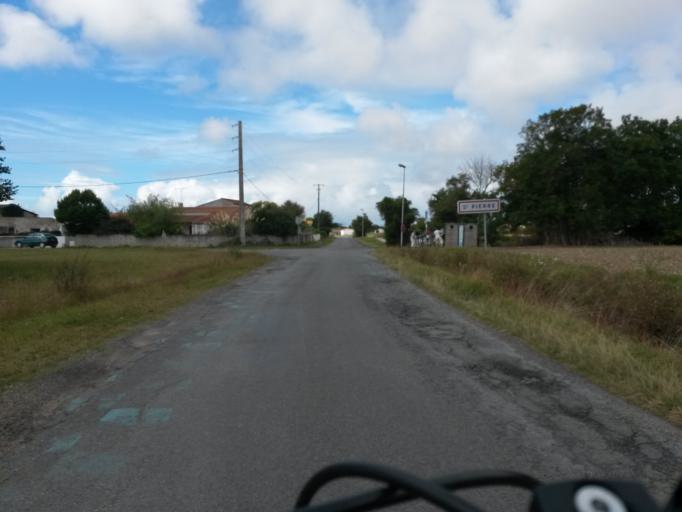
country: FR
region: Poitou-Charentes
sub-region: Departement de la Charente-Maritime
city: Dolus-d'Oleron
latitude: 45.9474
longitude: -1.2951
